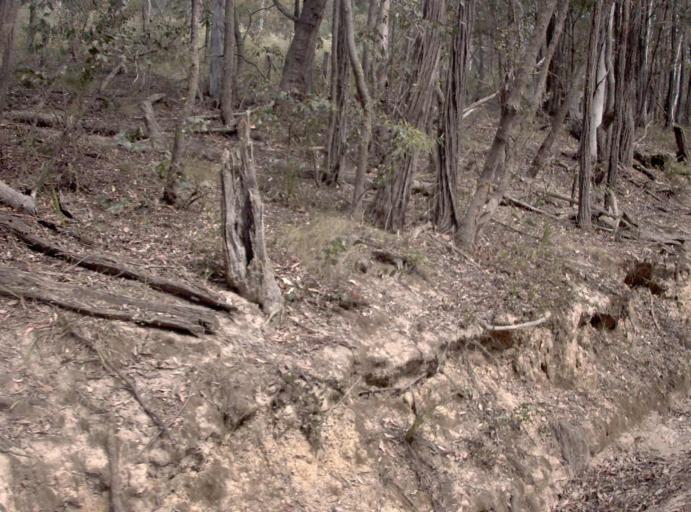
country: AU
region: New South Wales
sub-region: Bombala
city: Bombala
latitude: -37.1802
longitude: 148.6989
